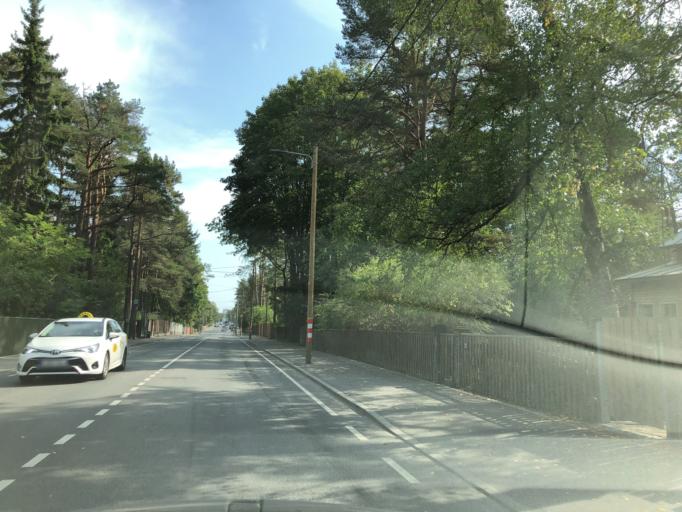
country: EE
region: Harju
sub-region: Tallinna linn
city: Tallinn
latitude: 59.3779
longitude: 24.7055
